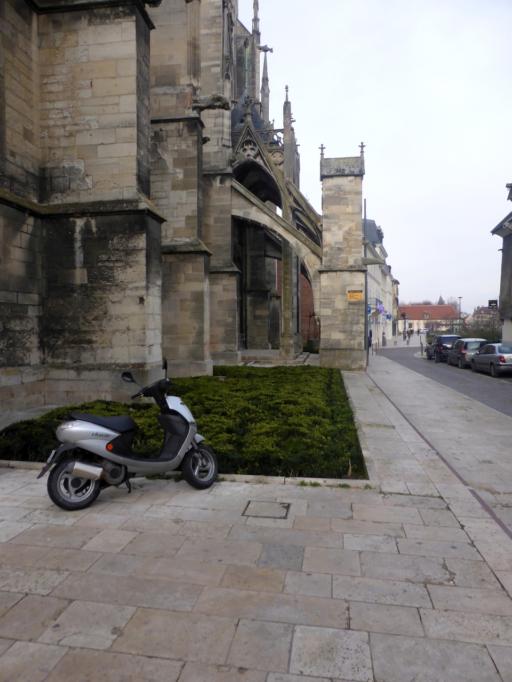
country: FR
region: Champagne-Ardenne
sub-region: Departement de l'Aube
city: Troyes
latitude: 48.2978
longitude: 4.0762
